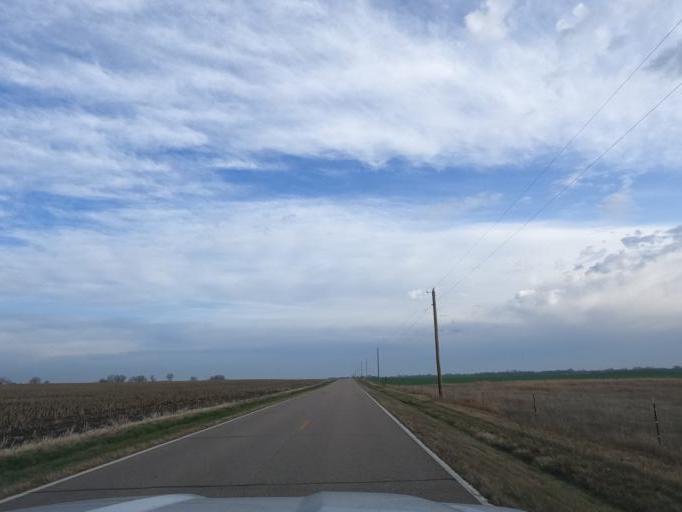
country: US
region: Kansas
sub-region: Reno County
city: Nickerson
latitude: 38.0299
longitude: -98.1787
